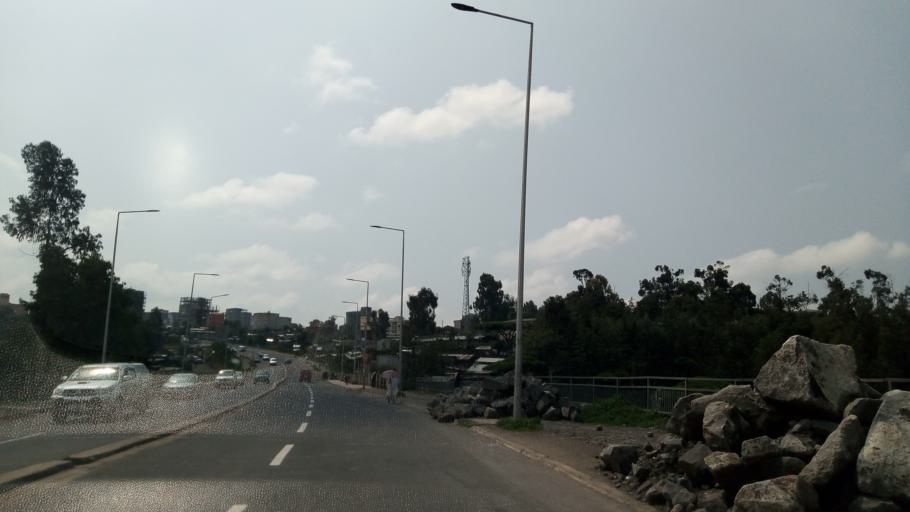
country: ET
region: Adis Abeba
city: Addis Ababa
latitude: 8.9823
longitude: 38.7688
